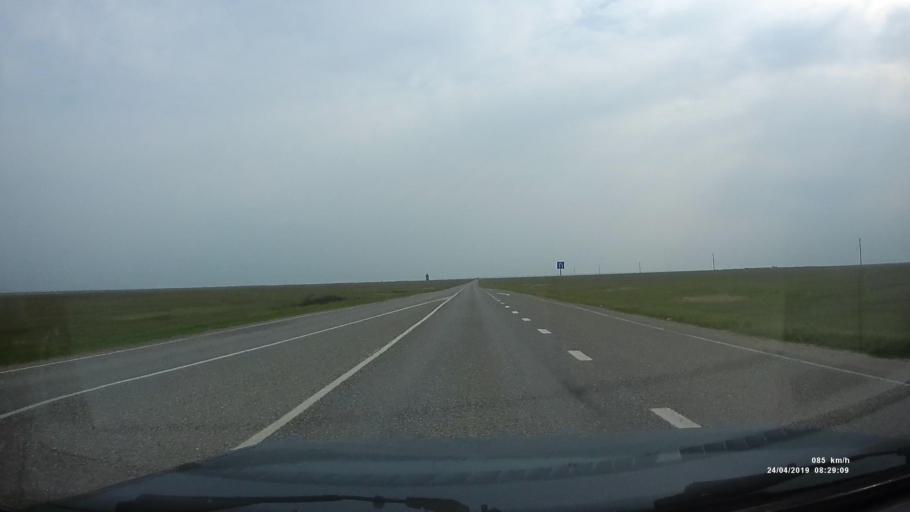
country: RU
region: Kalmykiya
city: Priyutnoye
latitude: 46.1499
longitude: 43.8263
